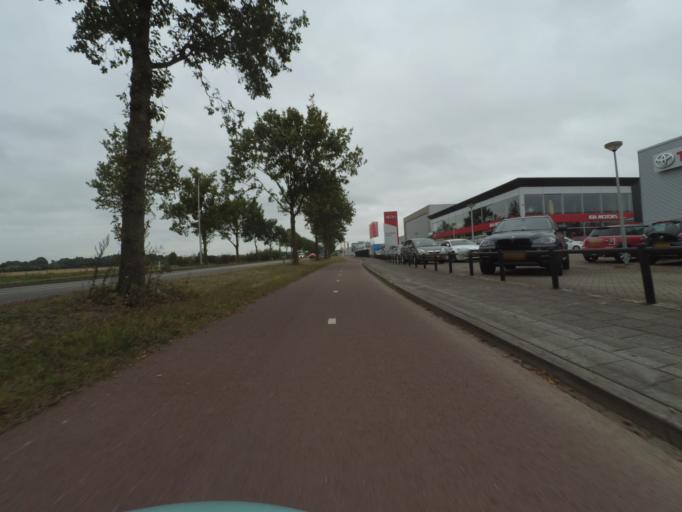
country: NL
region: Gelderland
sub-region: Gemeente Tiel
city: Tiel
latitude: 51.9077
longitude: 5.4265
